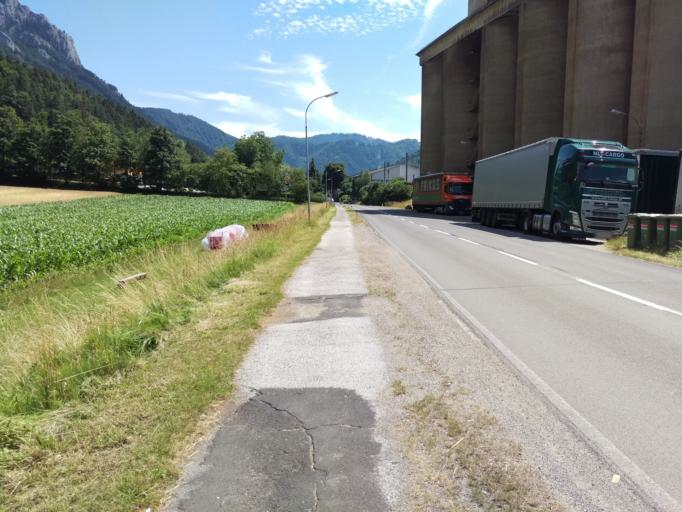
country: AT
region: Styria
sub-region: Politischer Bezirk Graz-Umgebung
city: Rothelstein
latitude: 47.3340
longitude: 15.3593
